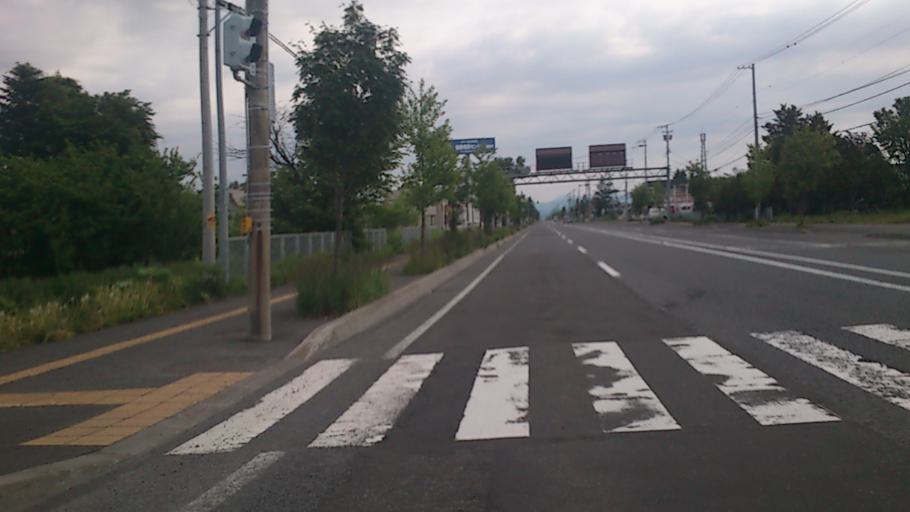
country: JP
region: Hokkaido
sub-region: Asahikawa-shi
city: Asahikawa
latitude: 43.8180
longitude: 142.4458
